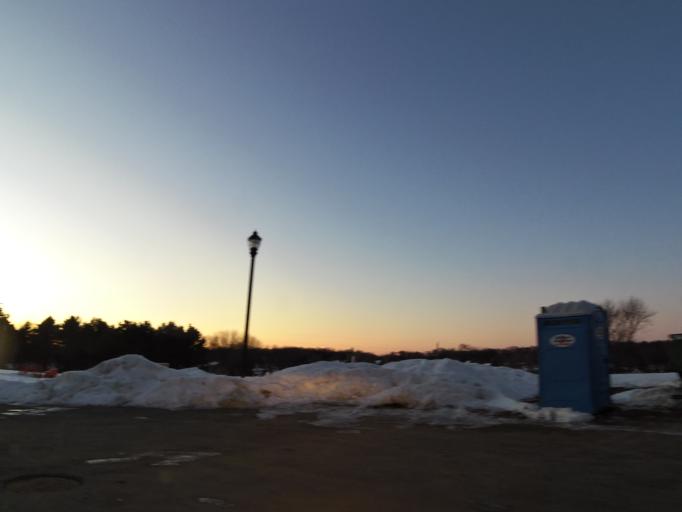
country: US
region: Minnesota
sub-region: Washington County
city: Lake Elmo
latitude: 45.0100
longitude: -92.8821
